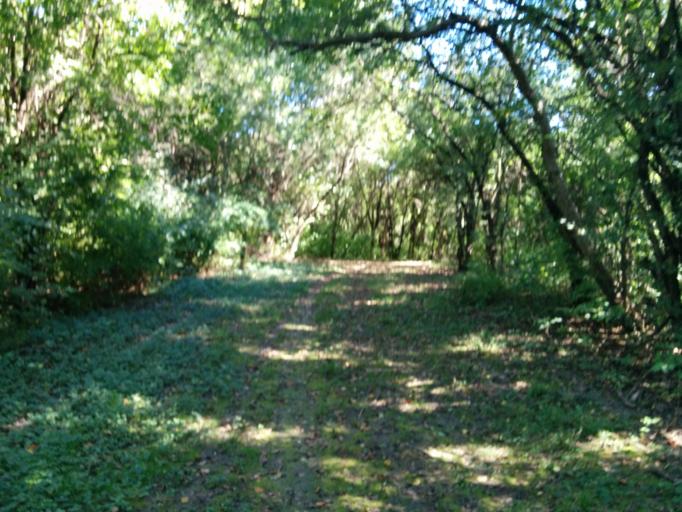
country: US
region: Illinois
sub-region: Cook County
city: Western Springs
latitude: 41.8211
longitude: -87.9111
